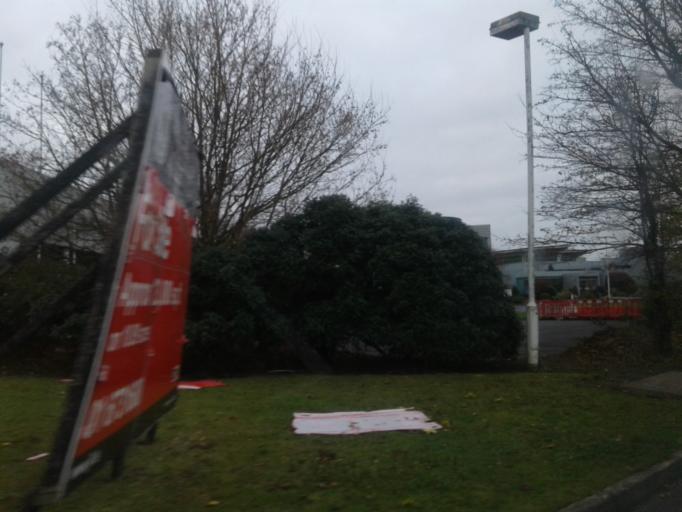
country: IE
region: Leinster
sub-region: Fingal County
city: Blanchardstown
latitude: 53.4080
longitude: -6.3544
